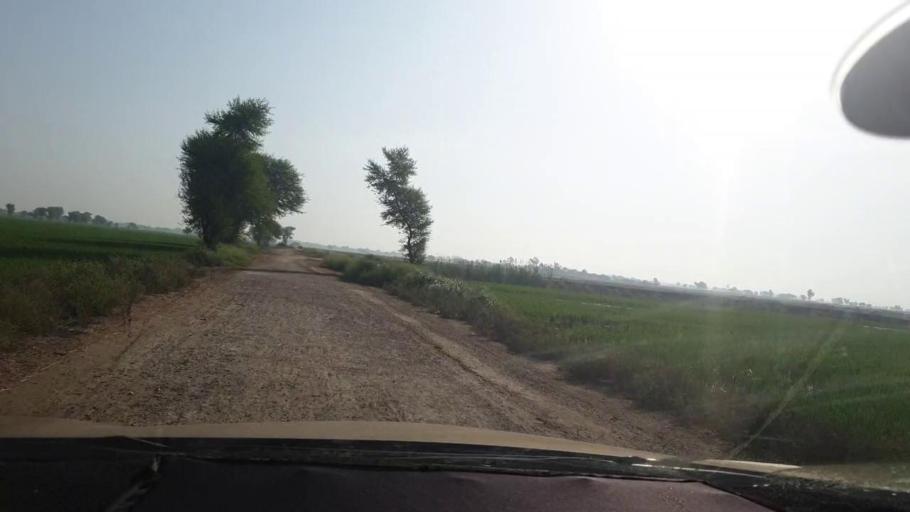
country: PK
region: Sindh
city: Kambar
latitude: 27.6417
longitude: 68.0454
